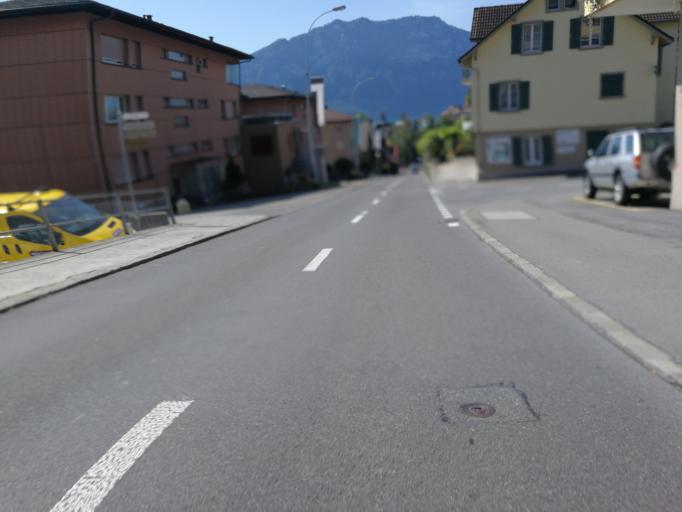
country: CH
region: Lucerne
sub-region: Lucerne-Land District
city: Weggis
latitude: 47.0337
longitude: 8.4251
